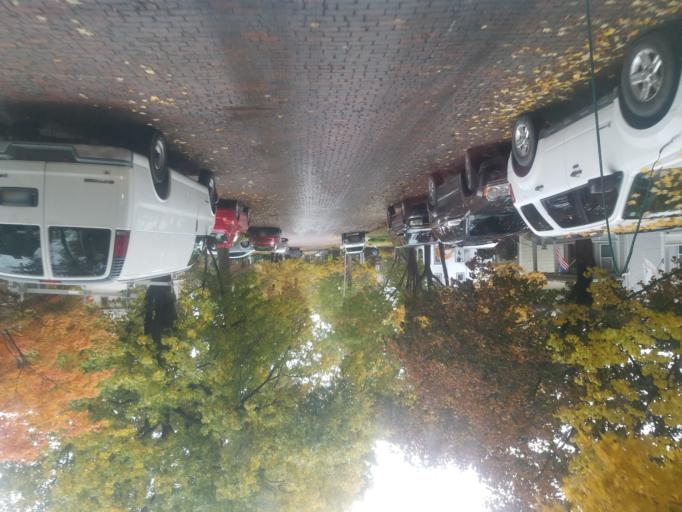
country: US
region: Ohio
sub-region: Washington County
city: Marietta
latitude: 39.4230
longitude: -81.4541
